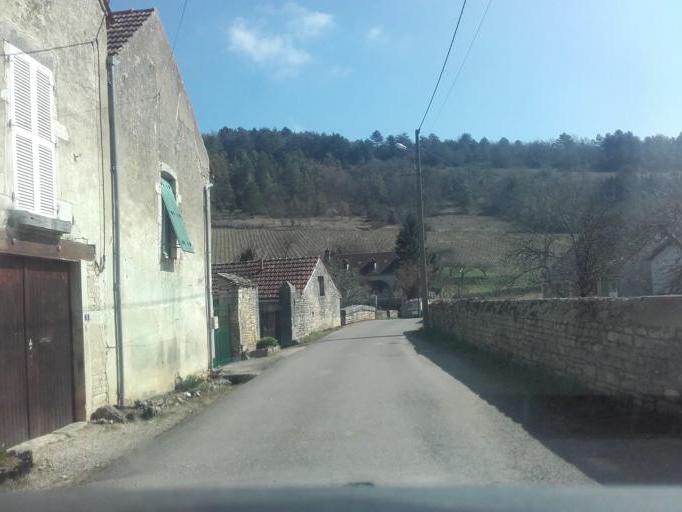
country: FR
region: Bourgogne
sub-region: Departement de la Cote-d'Or
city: Meursault
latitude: 47.0323
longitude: 4.7610
